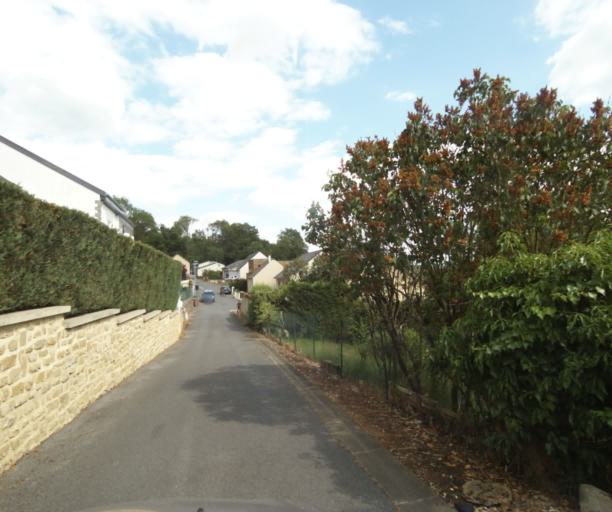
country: FR
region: Champagne-Ardenne
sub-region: Departement des Ardennes
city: Villers-Semeuse
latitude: 49.7574
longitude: 4.7501
